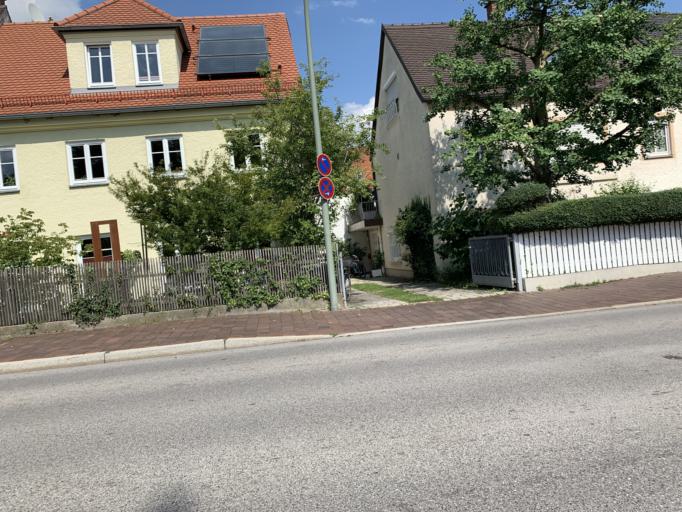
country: DE
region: Bavaria
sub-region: Upper Bavaria
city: Freising
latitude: 48.4018
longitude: 11.7410
